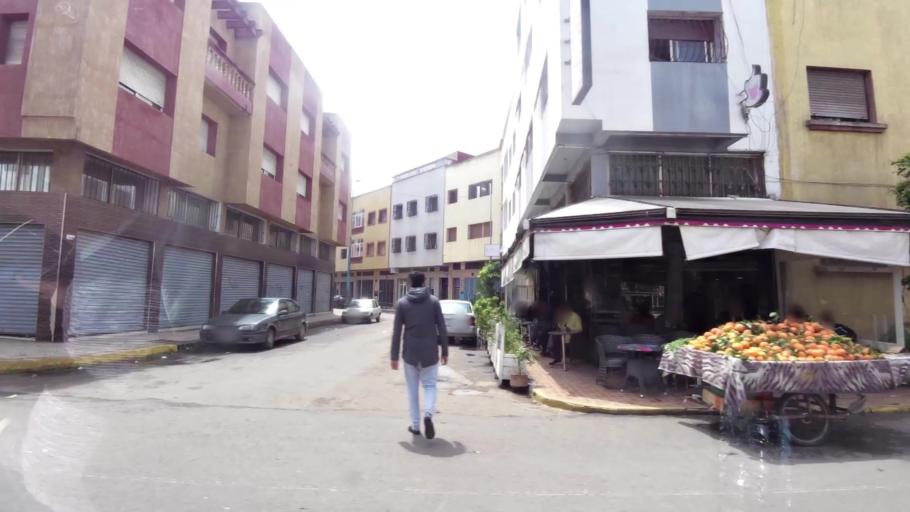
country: MA
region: Grand Casablanca
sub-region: Casablanca
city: Casablanca
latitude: 33.5475
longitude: -7.6823
